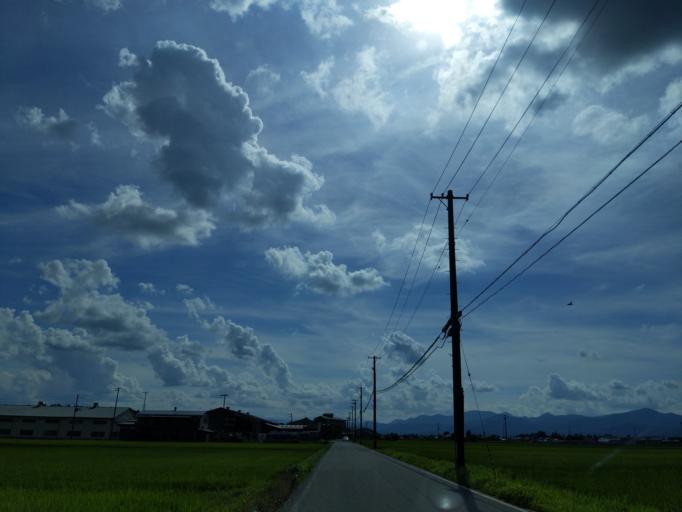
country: JP
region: Fukushima
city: Koriyama
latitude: 37.3634
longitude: 140.3476
